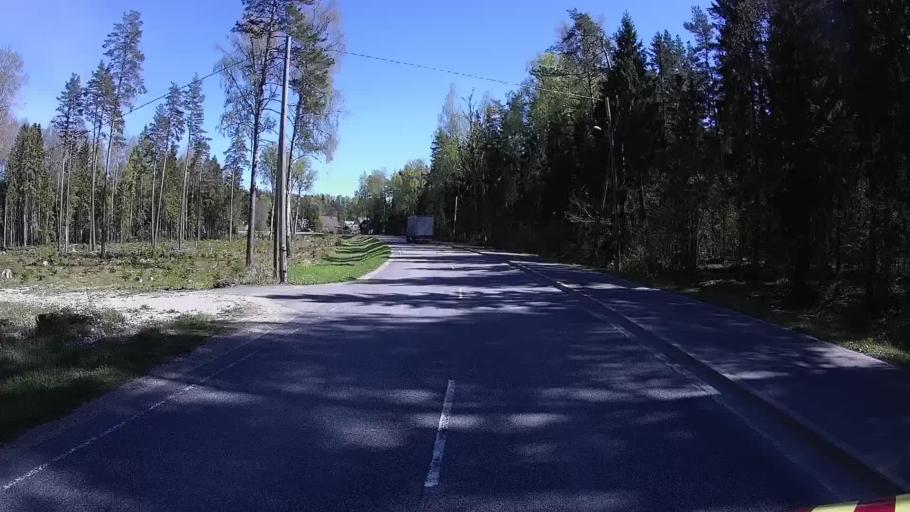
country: EE
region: Harju
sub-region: Kuusalu vald
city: Kuusalu
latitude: 59.2716
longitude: 25.6354
